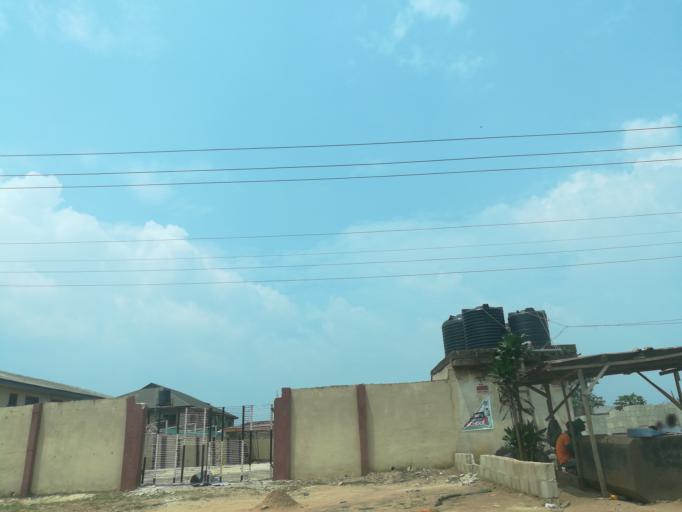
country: NG
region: Lagos
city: Ikorodu
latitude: 6.6061
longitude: 3.5974
